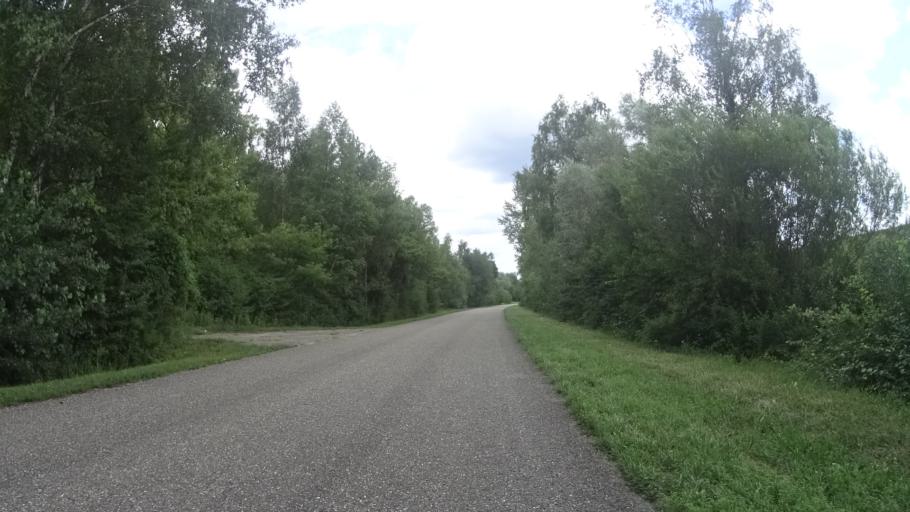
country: DE
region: Baden-Wuerttemberg
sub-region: Karlsruhe Region
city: Schwarzach
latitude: 48.7924
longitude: 8.0486
